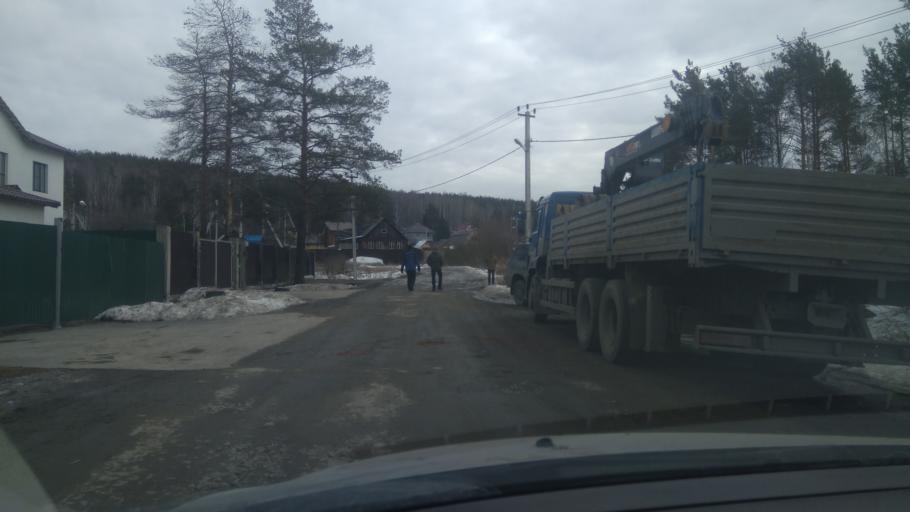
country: RU
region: Sverdlovsk
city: Severka
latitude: 56.8525
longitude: 60.3814
